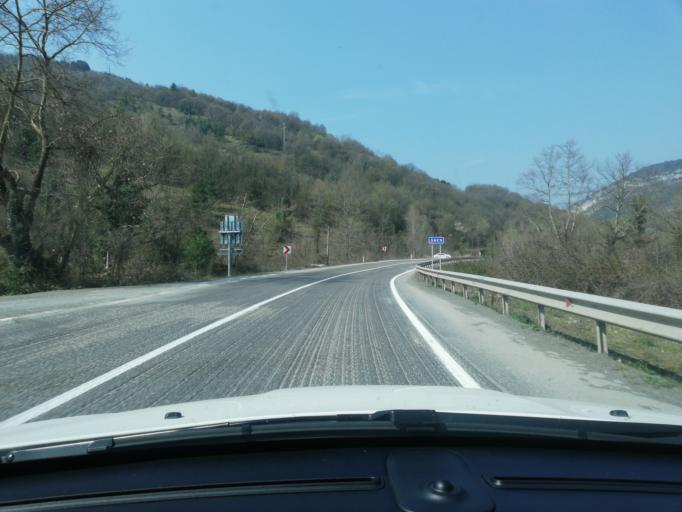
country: TR
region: Karabuk
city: Yenice
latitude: 41.2152
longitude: 32.2534
